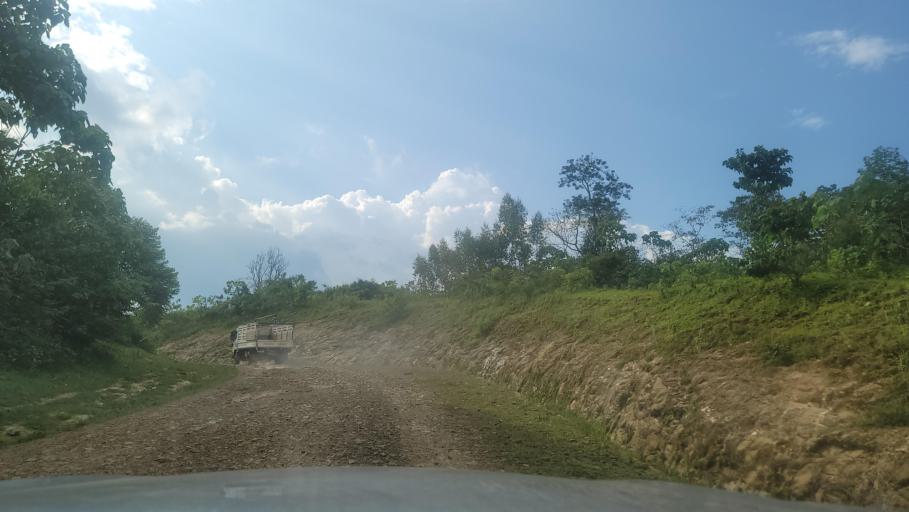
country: ET
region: Southern Nations, Nationalities, and People's Region
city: Bonga
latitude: 7.5784
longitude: 36.1598
